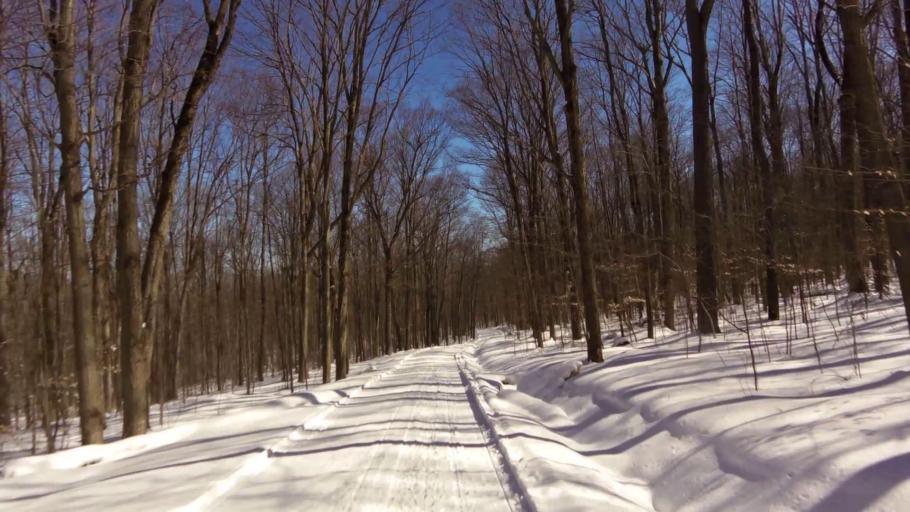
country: US
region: New York
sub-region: Allegany County
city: Houghton
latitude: 42.3426
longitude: -78.2010
